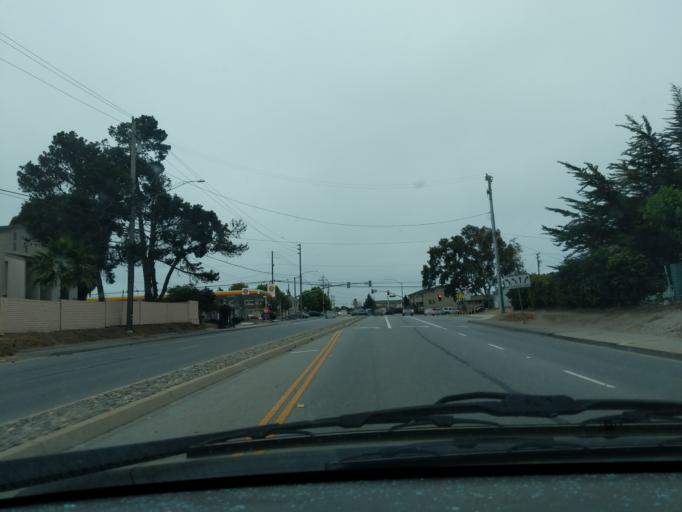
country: US
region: California
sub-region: Monterey County
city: Salinas
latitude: 36.6840
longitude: -121.6217
